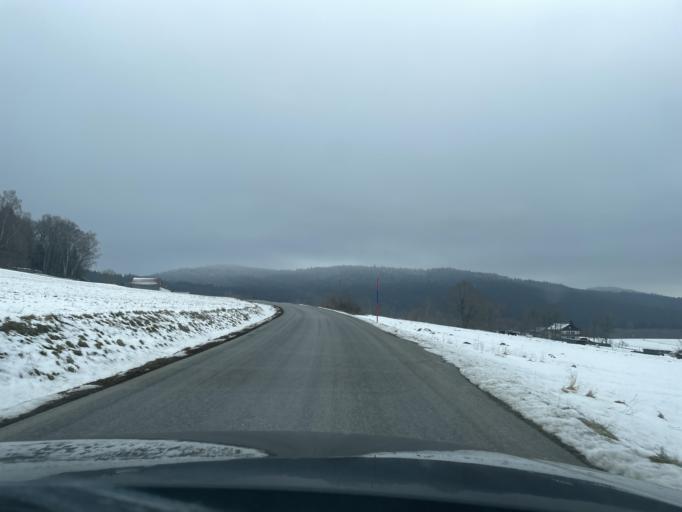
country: DE
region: Bavaria
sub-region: Upper Palatinate
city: Kotzting
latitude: 49.1431
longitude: 12.8903
